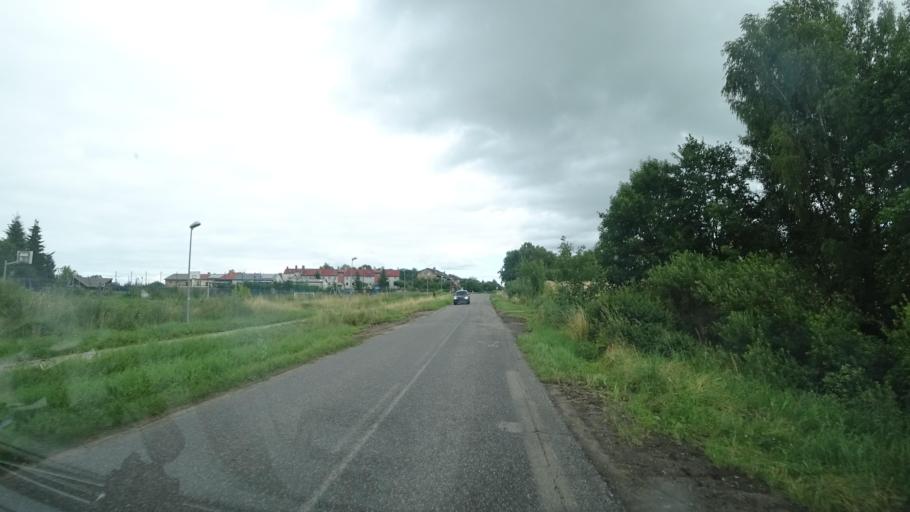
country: PL
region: Warmian-Masurian Voivodeship
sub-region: Powiat goldapski
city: Goldap
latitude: 54.3052
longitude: 22.4218
